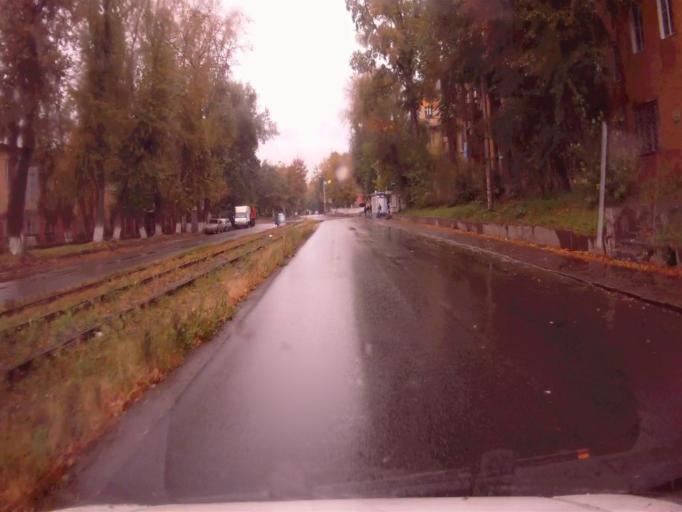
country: RU
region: Chelyabinsk
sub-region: Gorod Chelyabinsk
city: Chelyabinsk
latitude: 55.1901
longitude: 61.4127
